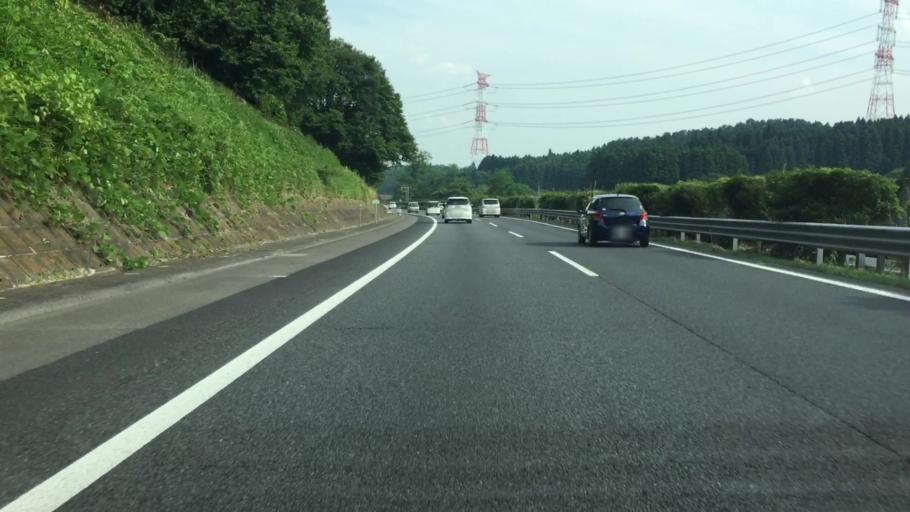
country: JP
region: Tochigi
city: Yaita
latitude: 36.7893
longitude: 139.9171
